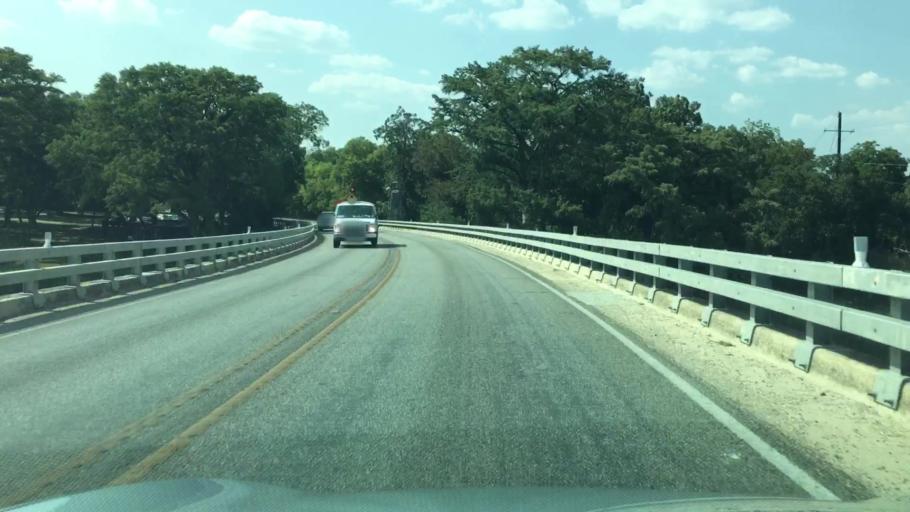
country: US
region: Texas
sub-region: Hays County
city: Wimberley
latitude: 29.9933
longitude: -98.0884
